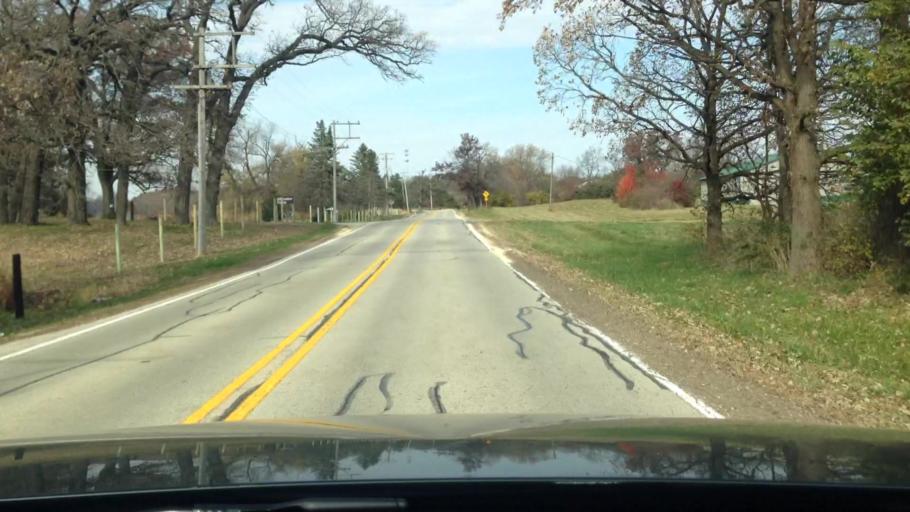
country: US
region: Illinois
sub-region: McHenry County
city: Woodstock
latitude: 42.2565
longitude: -88.4470
